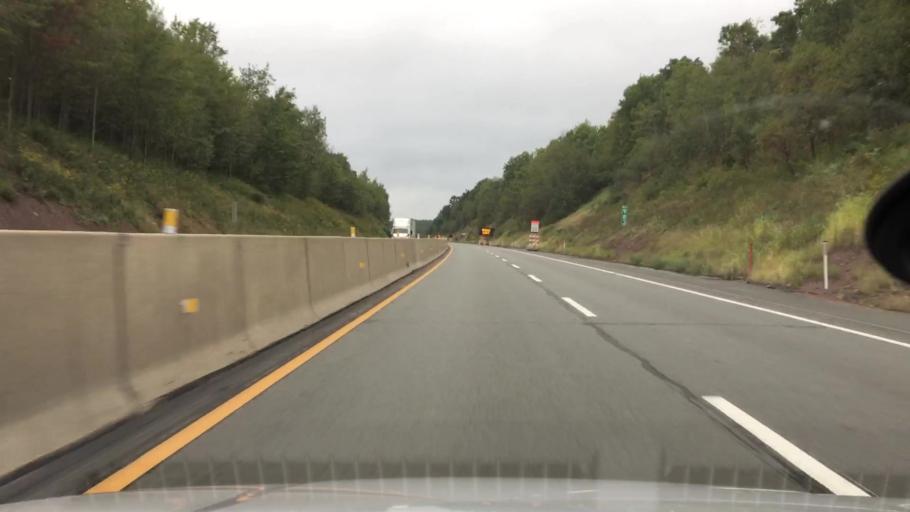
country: US
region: Pennsylvania
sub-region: Luzerne County
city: White Haven
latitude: 41.1069
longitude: -75.7518
